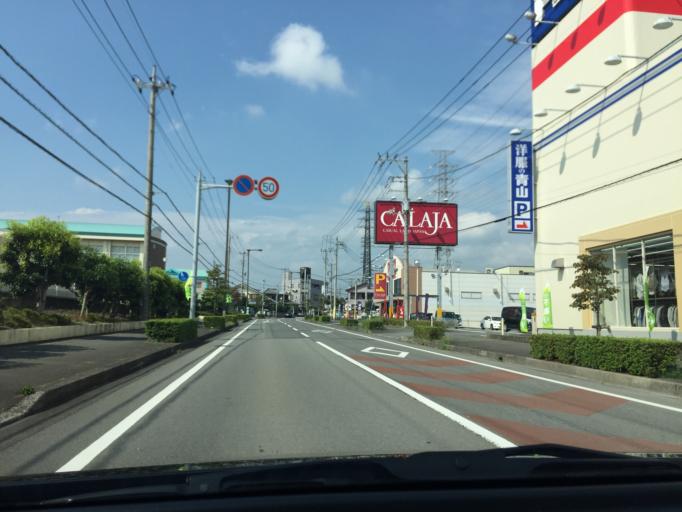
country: JP
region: Shizuoka
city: Mishima
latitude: 35.1554
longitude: 138.9052
